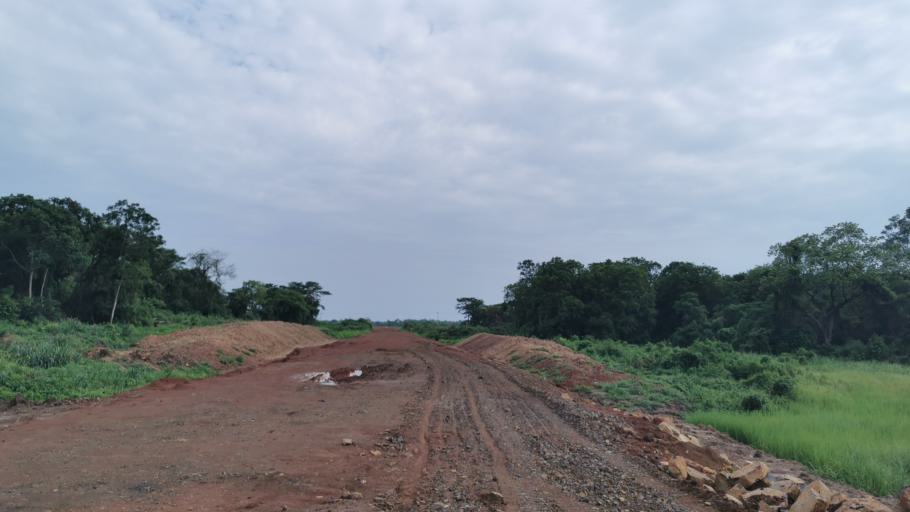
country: ET
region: Gambela
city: Gambela
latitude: 7.8665
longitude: 34.4933
